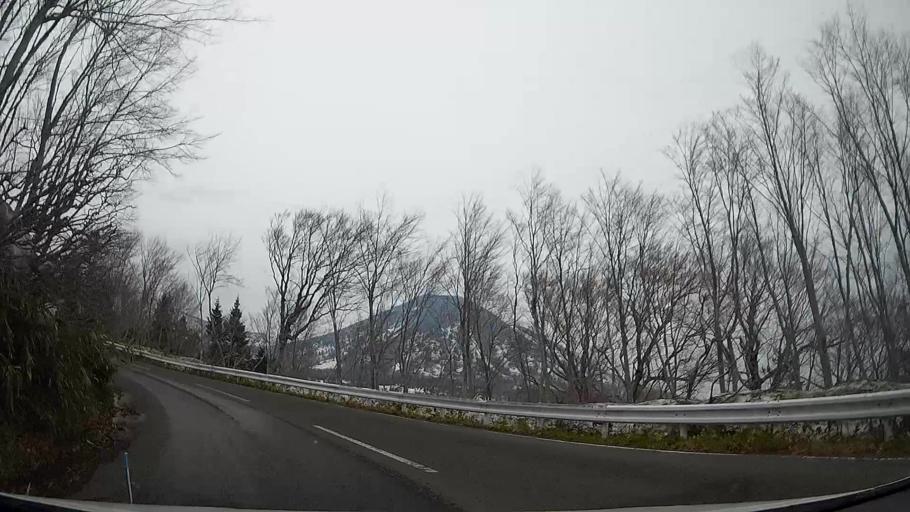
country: JP
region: Aomori
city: Aomori Shi
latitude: 40.6319
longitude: 140.9057
